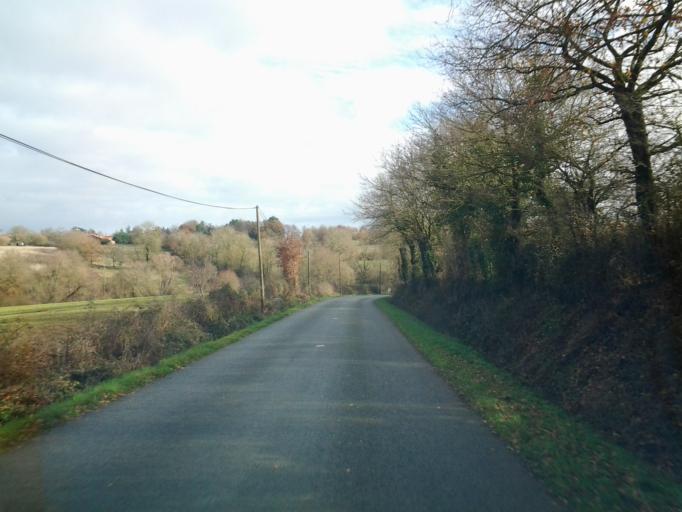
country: FR
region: Pays de la Loire
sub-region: Departement de la Vendee
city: Saint-Florent-des-Bois
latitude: 46.6286
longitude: -1.3238
